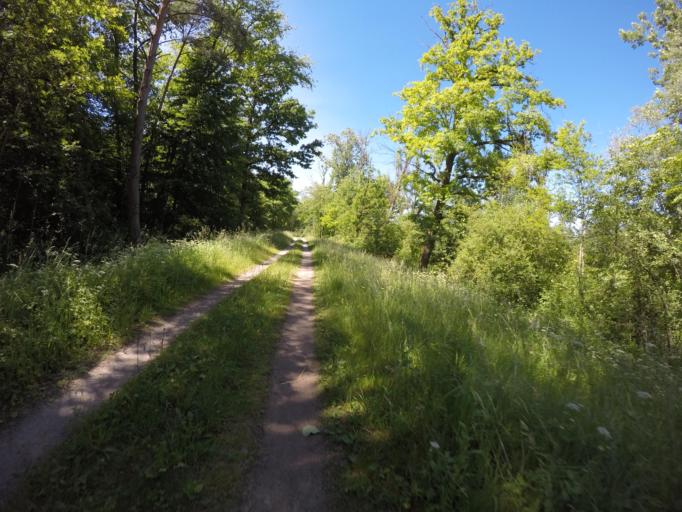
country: DE
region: Bavaria
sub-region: Upper Bavaria
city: Langenbach
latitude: 48.4615
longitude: 11.8817
